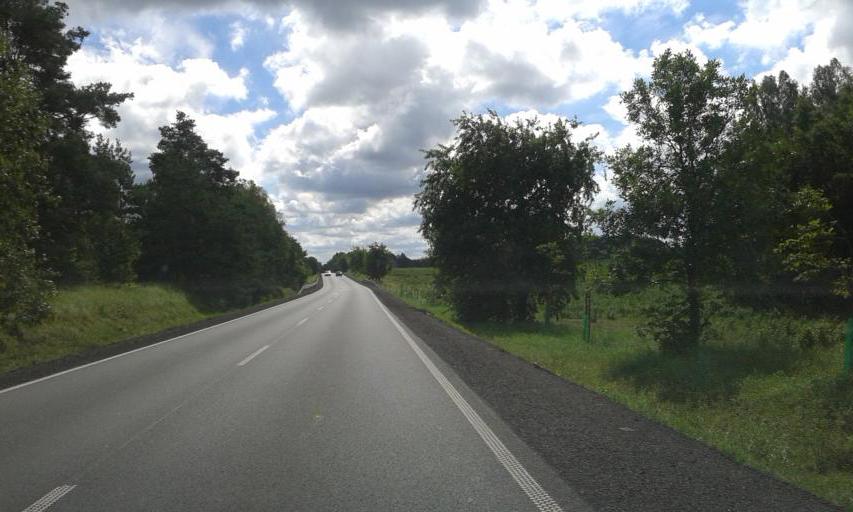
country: PL
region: West Pomeranian Voivodeship
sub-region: Powiat drawski
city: Czaplinek
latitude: 53.5364
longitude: 16.2790
